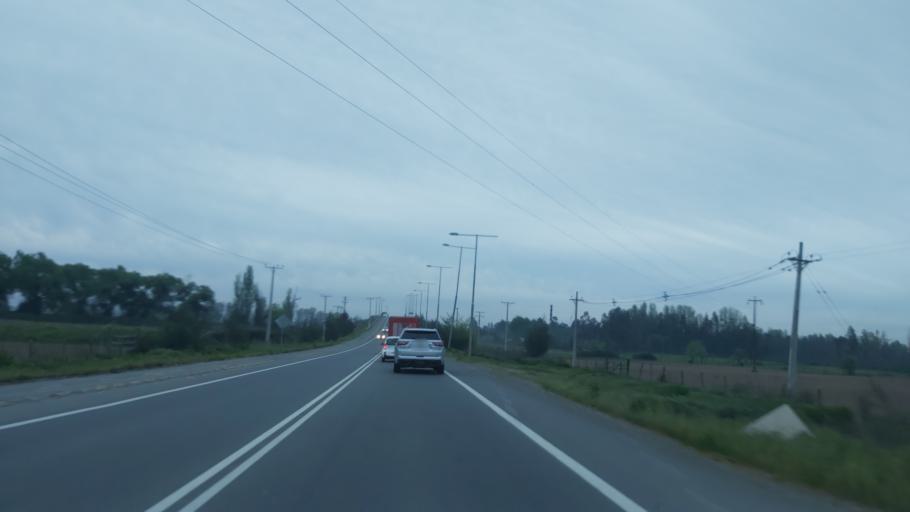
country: CL
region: Maule
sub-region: Provincia de Linares
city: Linares
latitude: -35.8247
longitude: -71.5965
